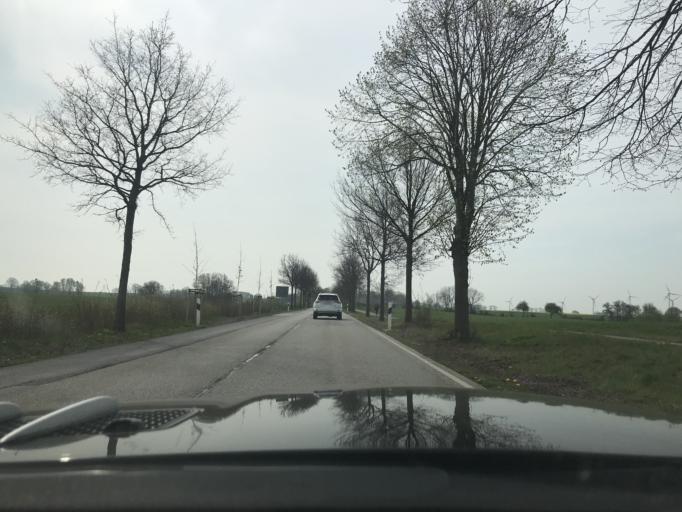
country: DE
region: Schleswig-Holstein
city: Heringsdorf
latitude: 54.2969
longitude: 11.0124
